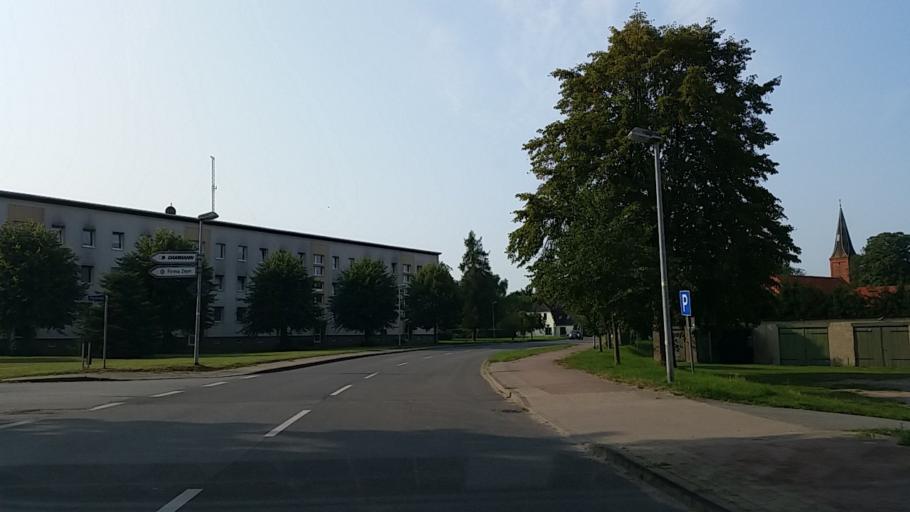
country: DE
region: Mecklenburg-Vorpommern
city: Lubtheen
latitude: 53.3799
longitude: 11.0810
